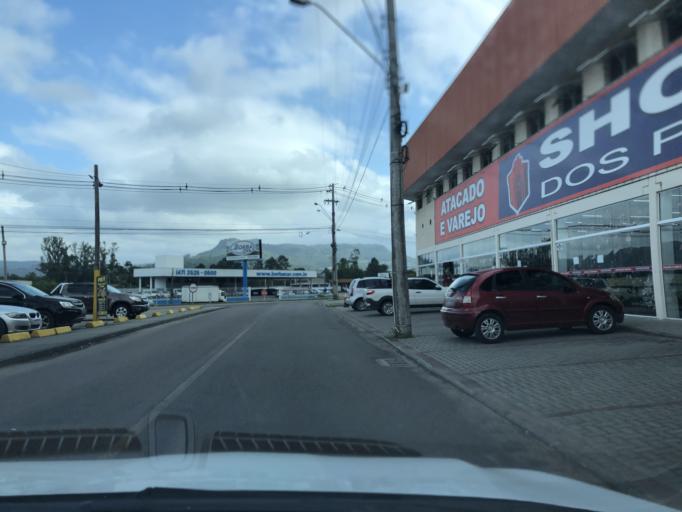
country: BR
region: Santa Catarina
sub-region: Rio Do Sul
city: Rio do Sul
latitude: -27.1933
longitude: -49.6246
